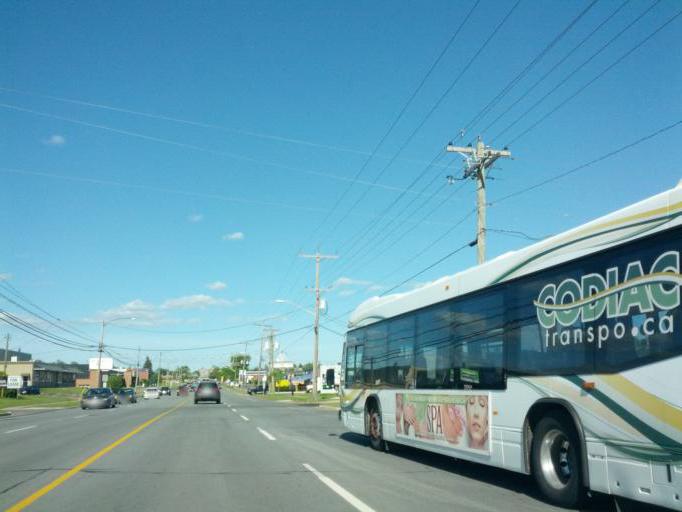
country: CA
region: New Brunswick
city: Moncton
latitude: 46.0850
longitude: -64.8115
